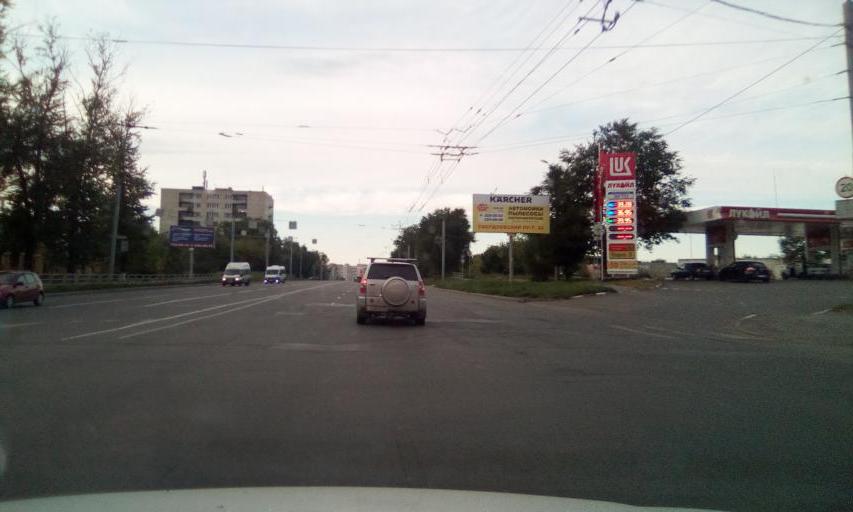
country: RU
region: Chelyabinsk
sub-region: Gorod Chelyabinsk
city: Chelyabinsk
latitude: 55.1614
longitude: 61.4516
